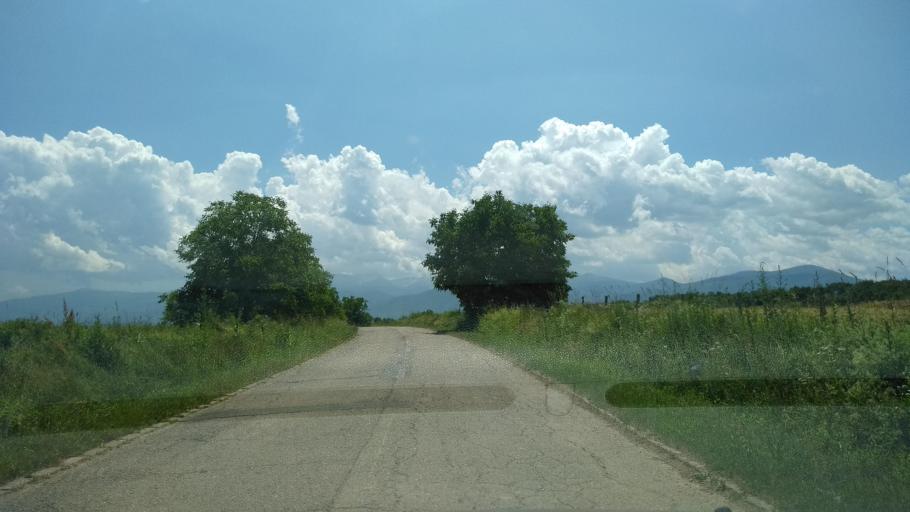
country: RO
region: Hunedoara
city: Densus
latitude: 45.5645
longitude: 22.8148
